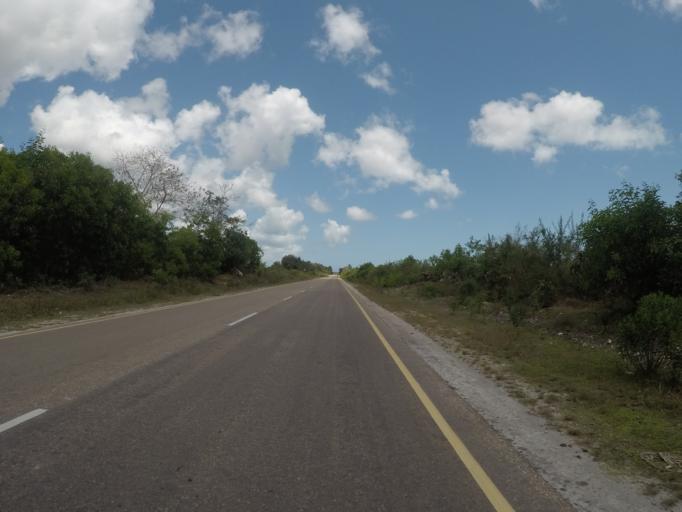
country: TZ
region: Zanzibar Central/South
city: Koani
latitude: -6.2621
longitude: 39.3595
